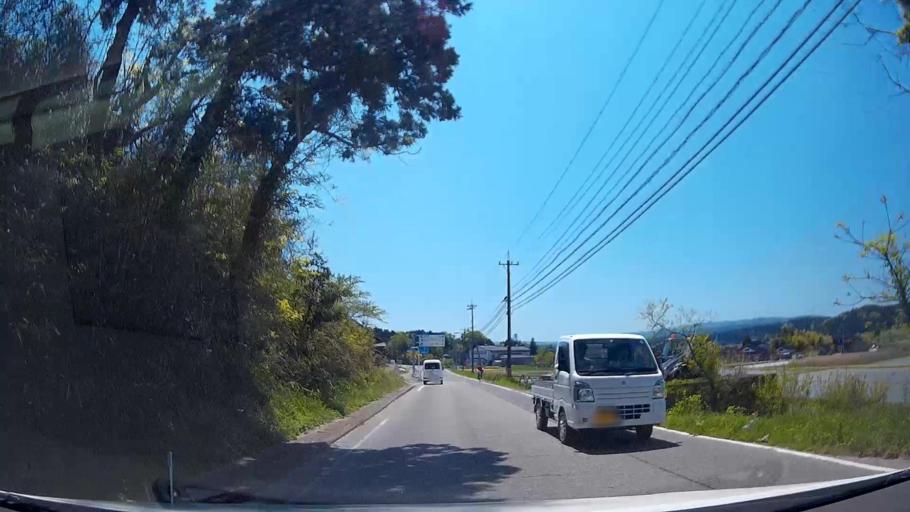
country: JP
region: Ishikawa
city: Nanao
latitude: 37.4518
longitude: 137.2987
